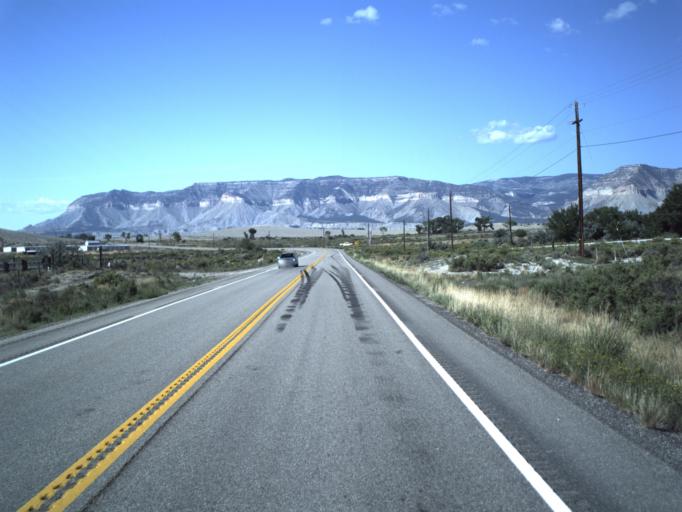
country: US
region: Utah
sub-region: Emery County
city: Ferron
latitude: 39.1178
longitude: -111.1201
